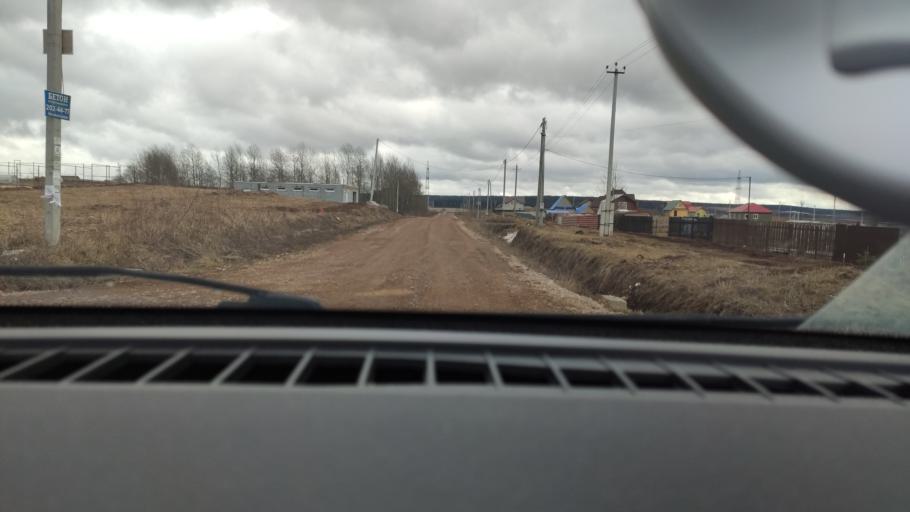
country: RU
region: Perm
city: Ferma
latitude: 57.9463
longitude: 56.3424
